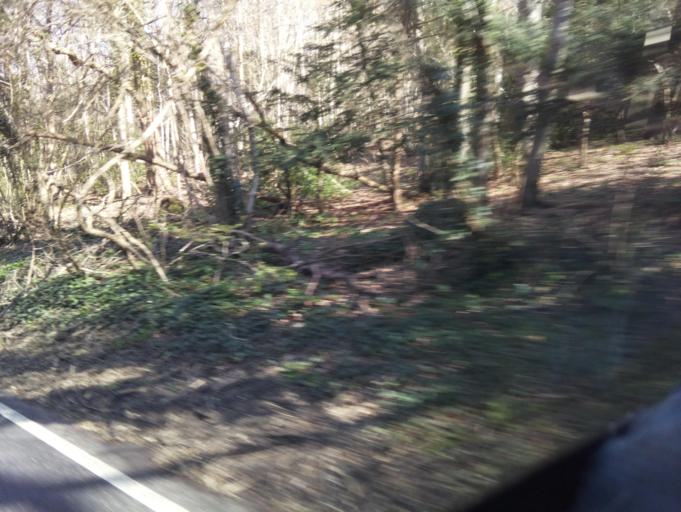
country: GB
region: England
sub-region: Bath and North East Somerset
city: Freshford
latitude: 51.3819
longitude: -2.2966
